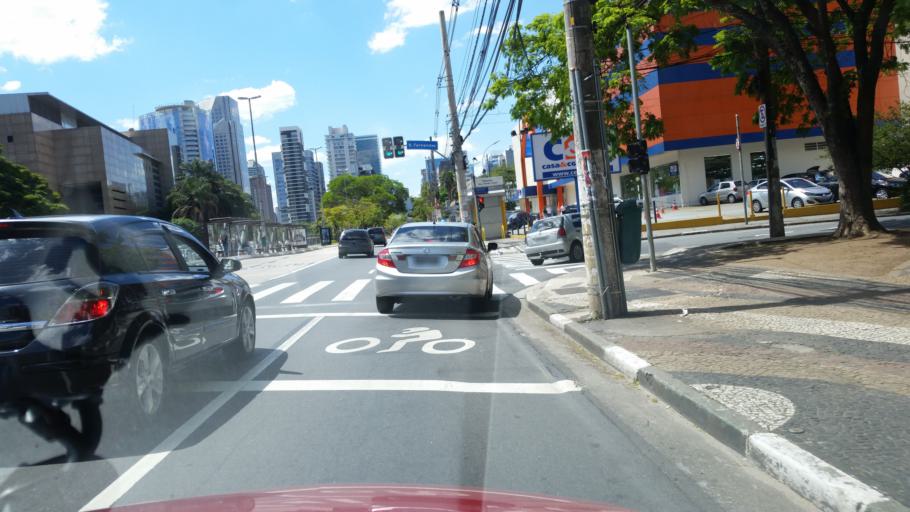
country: BR
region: Sao Paulo
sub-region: Sao Paulo
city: Sao Paulo
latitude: -23.6178
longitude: -46.6973
